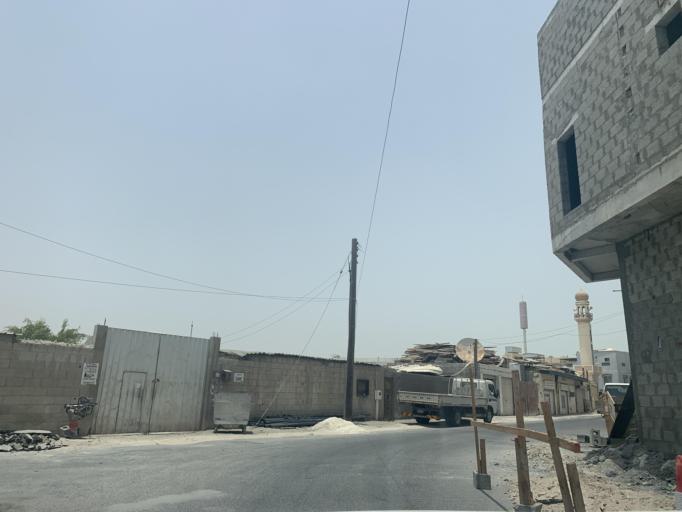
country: BH
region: Manama
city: Jidd Hafs
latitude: 26.2102
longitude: 50.5423
